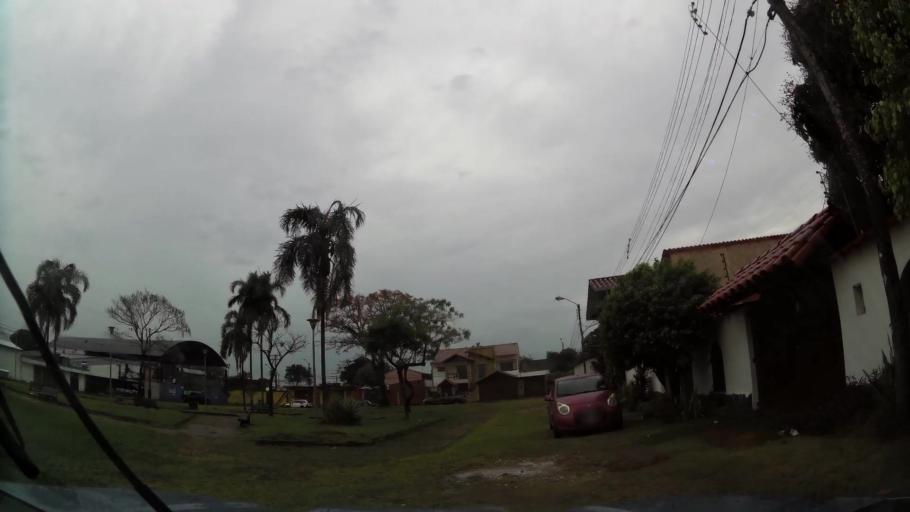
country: BO
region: Santa Cruz
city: Santa Cruz de la Sierra
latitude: -17.7899
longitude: -63.2122
